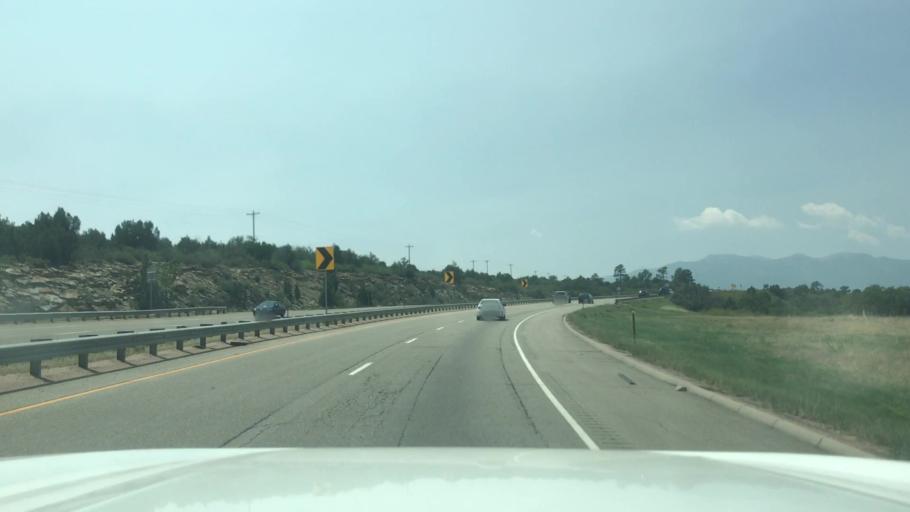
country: US
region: Colorado
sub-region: Pueblo County
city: Colorado City
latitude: 37.9398
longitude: -104.8077
